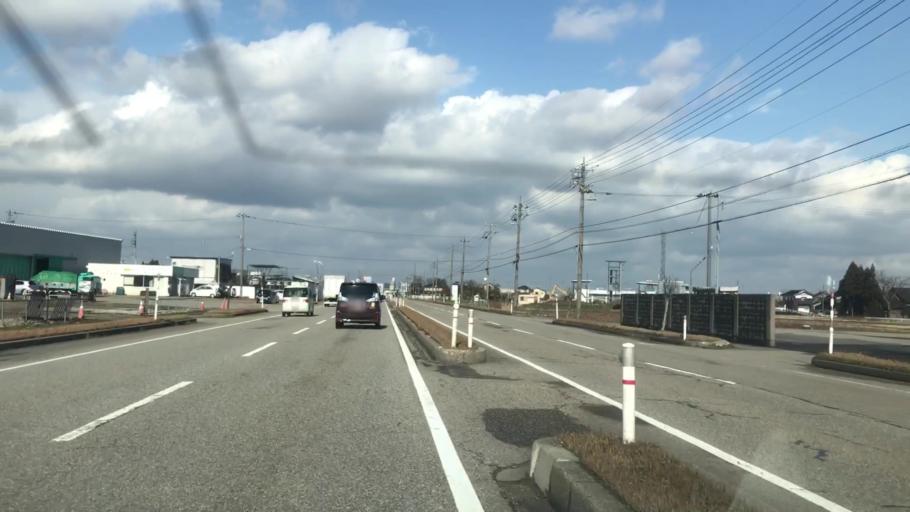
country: JP
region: Toyama
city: Kuragaki-kosugi
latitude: 36.7118
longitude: 137.0808
